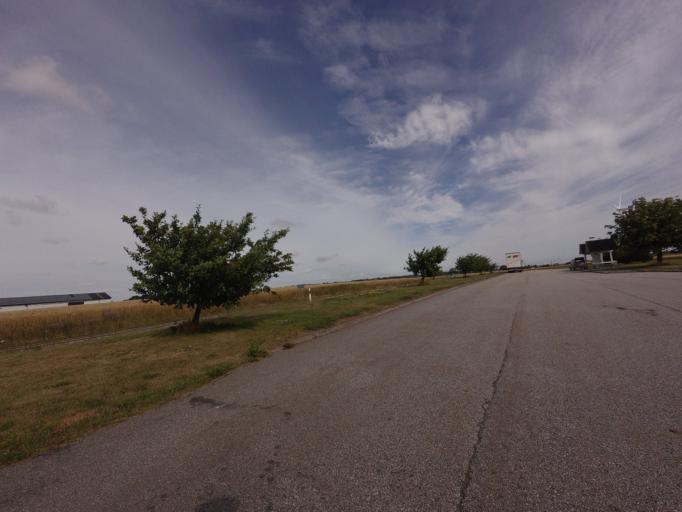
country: SE
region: Skane
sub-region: Simrishamns Kommun
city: Simrishamn
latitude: 55.5345
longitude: 14.3404
